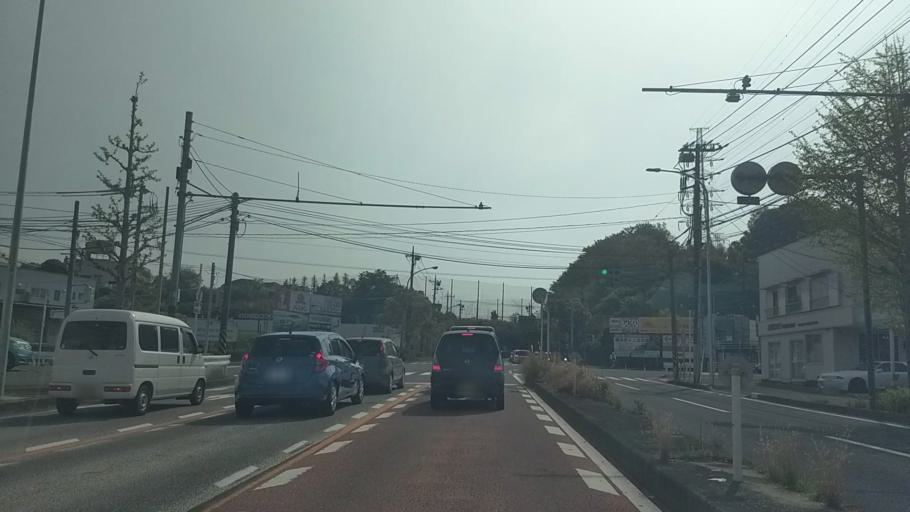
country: JP
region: Kanagawa
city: Yokohama
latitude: 35.3773
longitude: 139.6084
